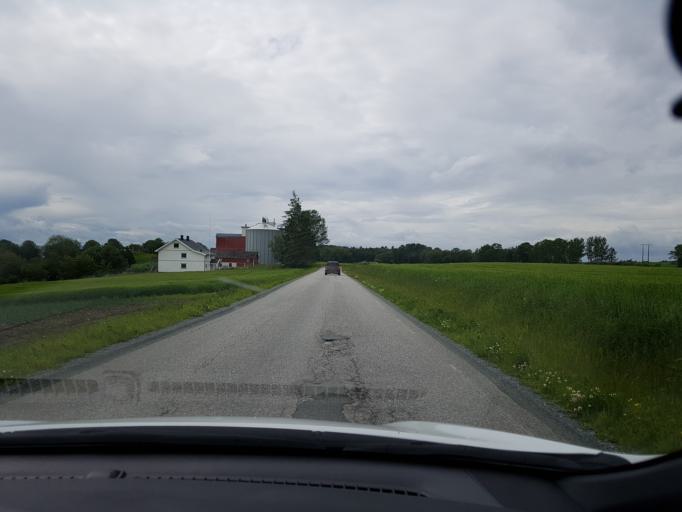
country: NO
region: Nord-Trondelag
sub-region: Frosta
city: Frosta
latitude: 63.5726
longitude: 10.7085
